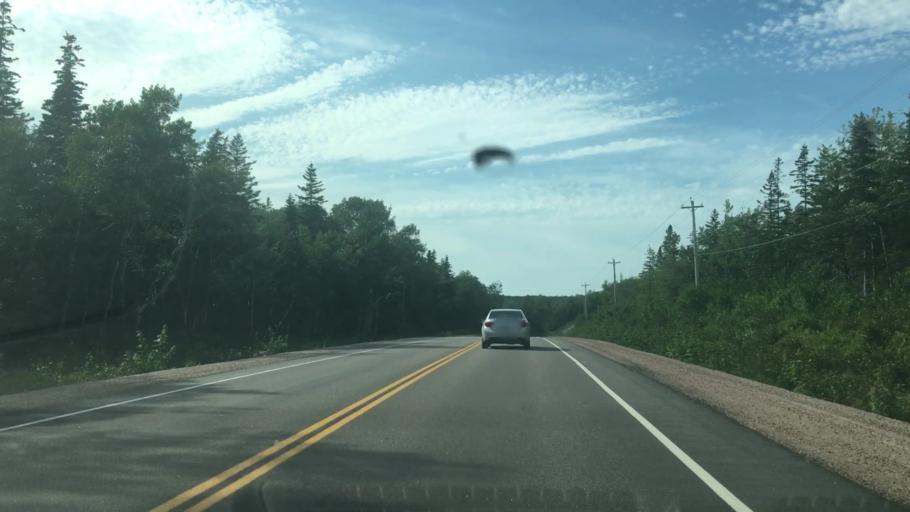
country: CA
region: Nova Scotia
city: Sydney Mines
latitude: 46.8198
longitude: -60.3521
